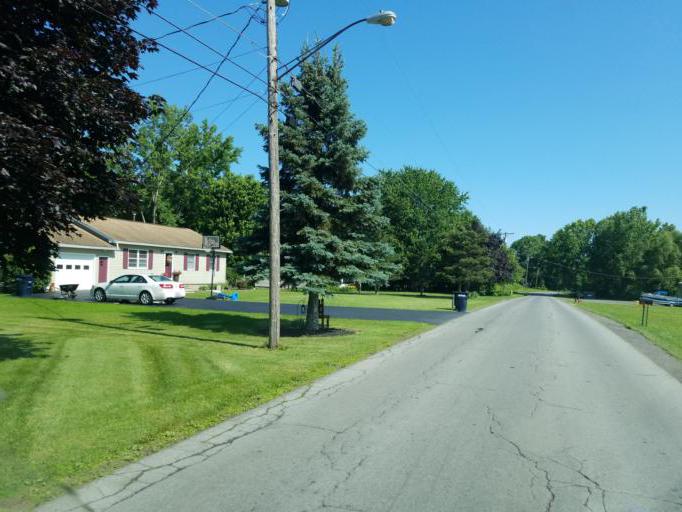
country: US
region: New York
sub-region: Wayne County
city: Clyde
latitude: 43.0739
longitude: -76.8761
